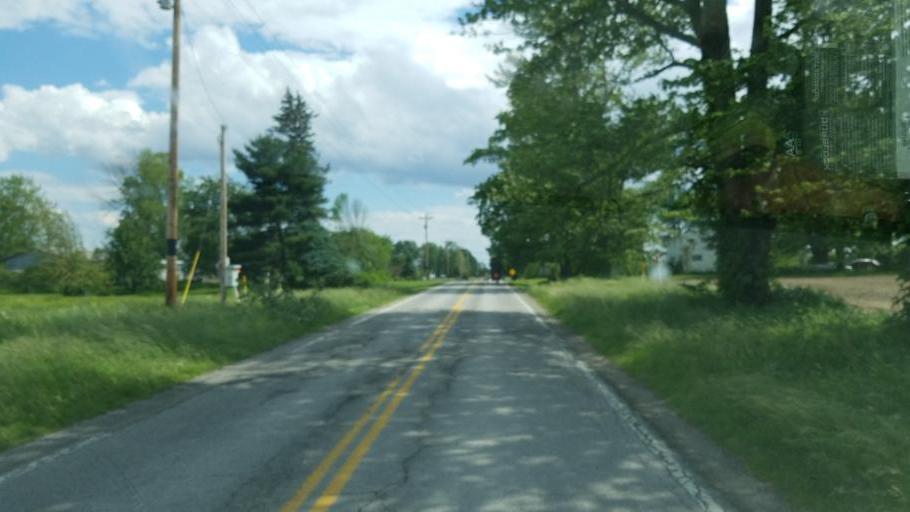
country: US
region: Ohio
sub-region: Huron County
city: Plymouth
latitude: 41.0345
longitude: -82.6080
